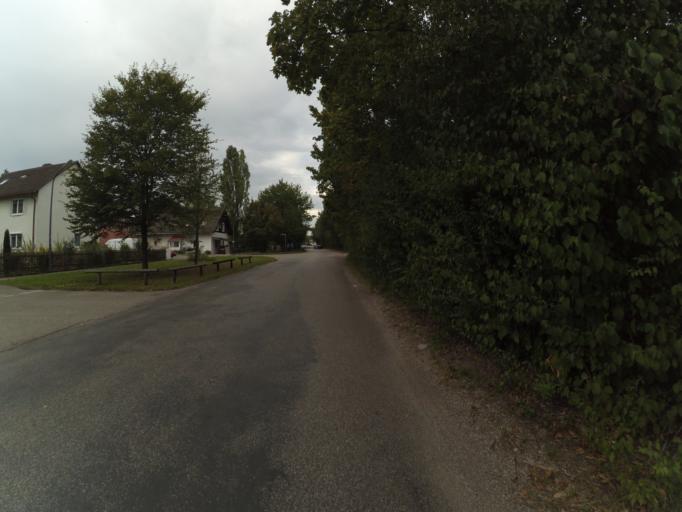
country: DE
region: Bavaria
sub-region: Upper Bavaria
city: Oberschleissheim
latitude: 48.1983
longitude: 11.5541
